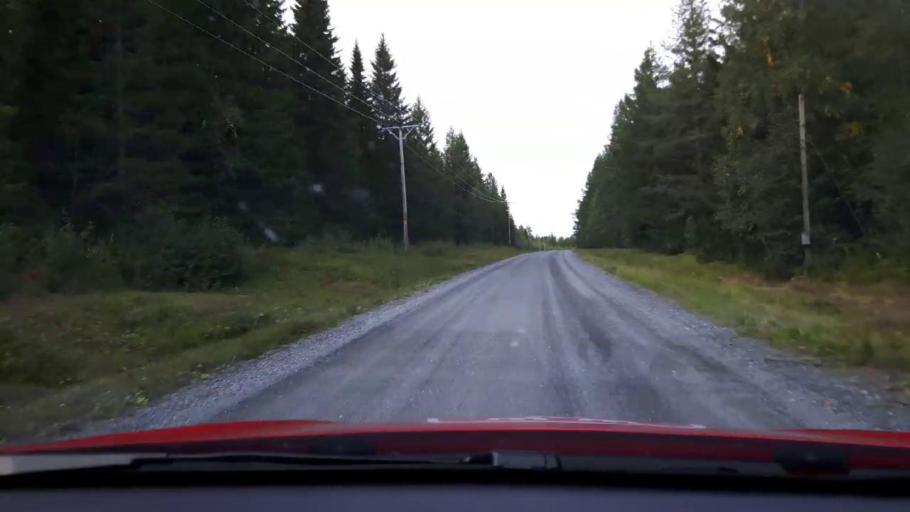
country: SE
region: Jaemtland
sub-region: Krokoms Kommun
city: Valla
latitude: 63.2439
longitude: 13.9729
